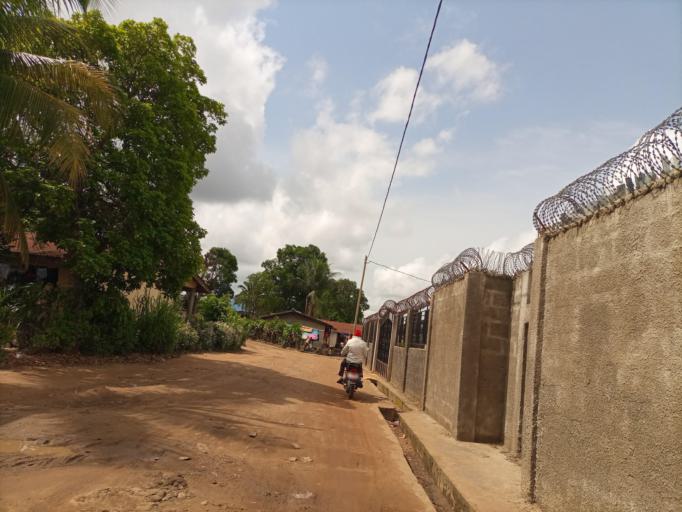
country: SL
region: Southern Province
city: Bo
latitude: 7.9639
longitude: -11.7606
